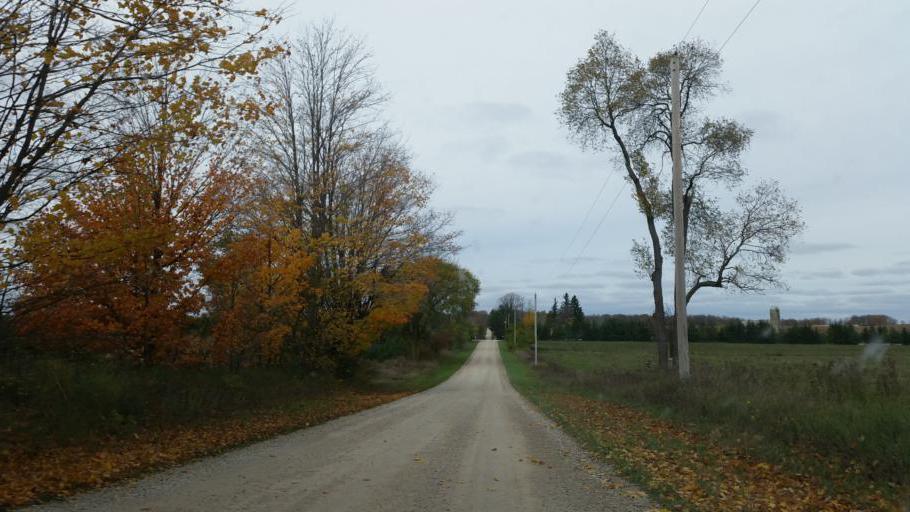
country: CA
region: Ontario
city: Wingham
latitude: 43.9906
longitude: -81.3362
